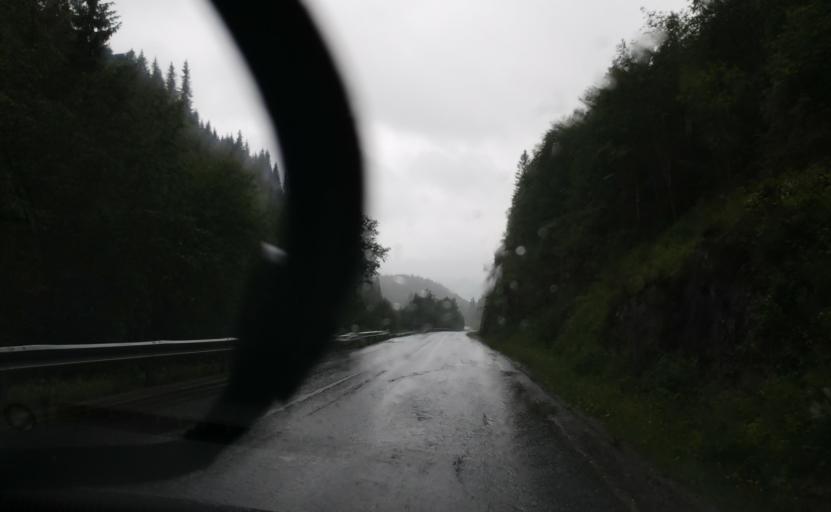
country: NO
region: Sor-Trondelag
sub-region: Selbu
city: Mebonden
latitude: 63.3214
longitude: 11.0849
